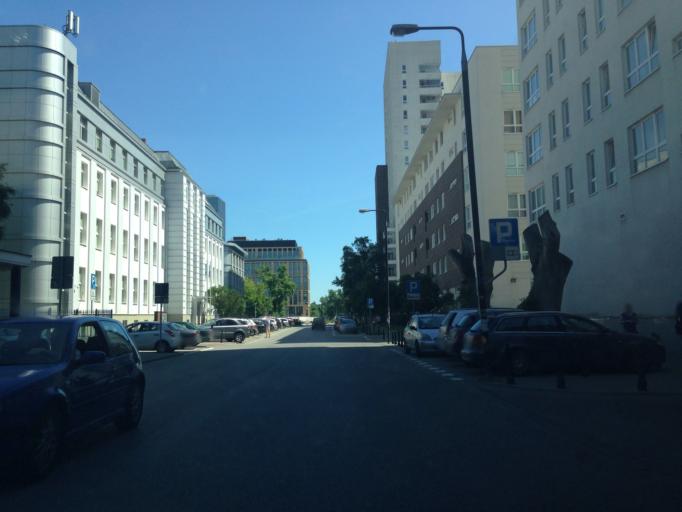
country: PL
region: Masovian Voivodeship
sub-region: Warszawa
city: Wola
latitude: 52.2542
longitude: 20.9904
